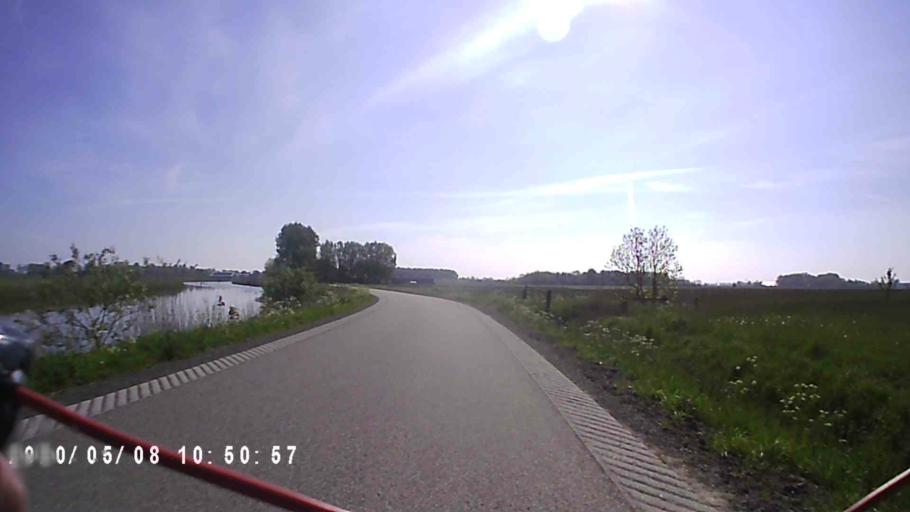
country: NL
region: Groningen
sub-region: Gemeente Bedum
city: Bedum
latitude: 53.3348
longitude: 6.5699
